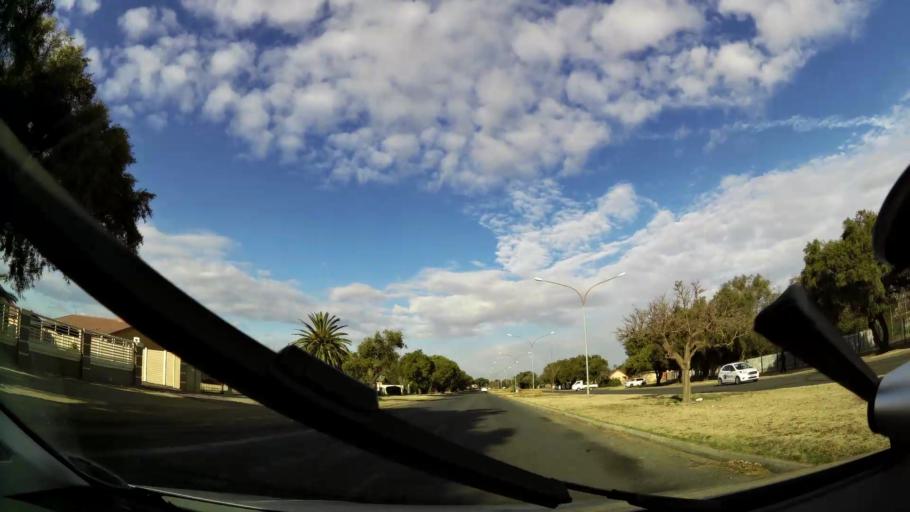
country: ZA
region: Orange Free State
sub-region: Lejweleputswa District Municipality
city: Welkom
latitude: -27.9882
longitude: 26.7420
